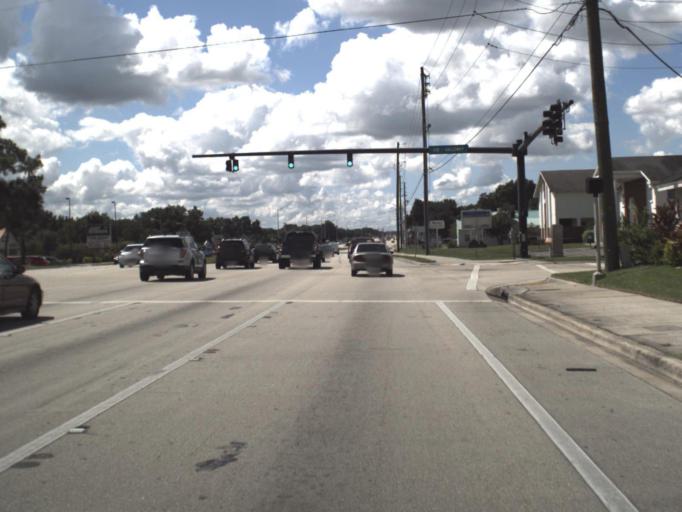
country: US
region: Florida
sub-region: Polk County
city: Gibsonia
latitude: 28.1139
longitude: -81.9739
